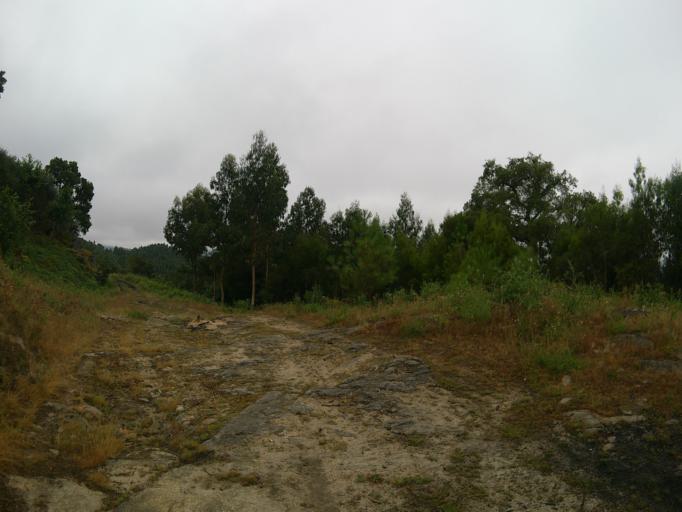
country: PT
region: Viana do Castelo
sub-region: Ponte de Lima
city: Ponte de Lima
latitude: 41.7236
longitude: -8.6095
